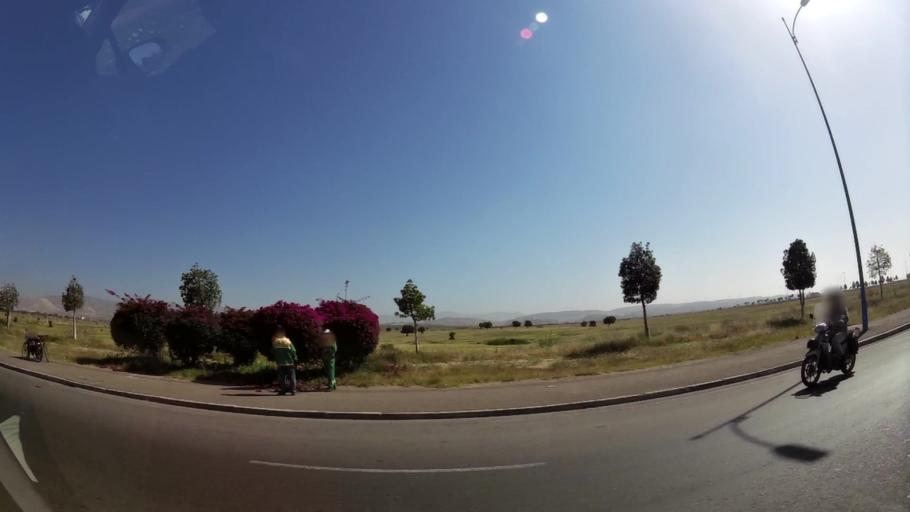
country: MA
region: Oued ed Dahab-Lagouira
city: Dakhla
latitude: 30.4122
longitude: -9.5430
